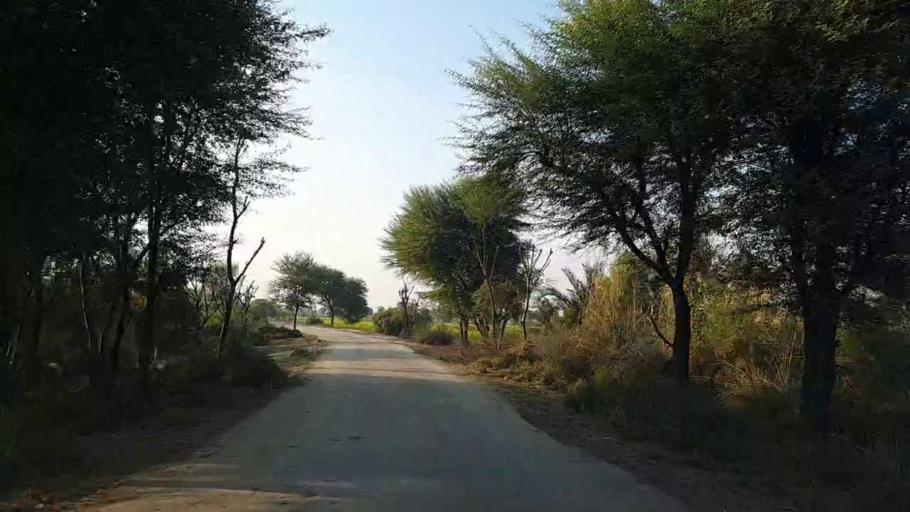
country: PK
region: Sindh
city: Jam Sahib
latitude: 26.3944
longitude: 68.5432
